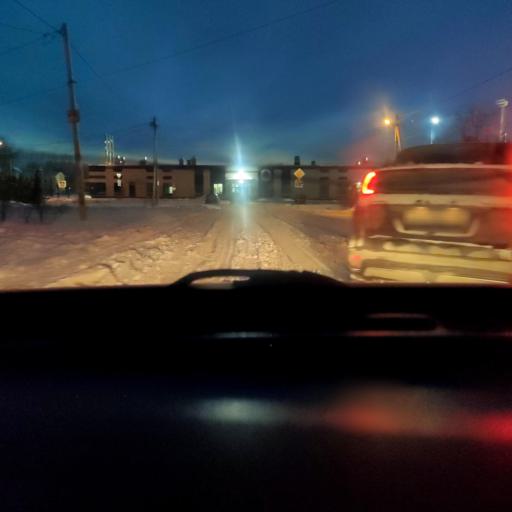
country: RU
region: Voronezj
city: Voronezh
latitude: 51.7337
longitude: 39.2620
